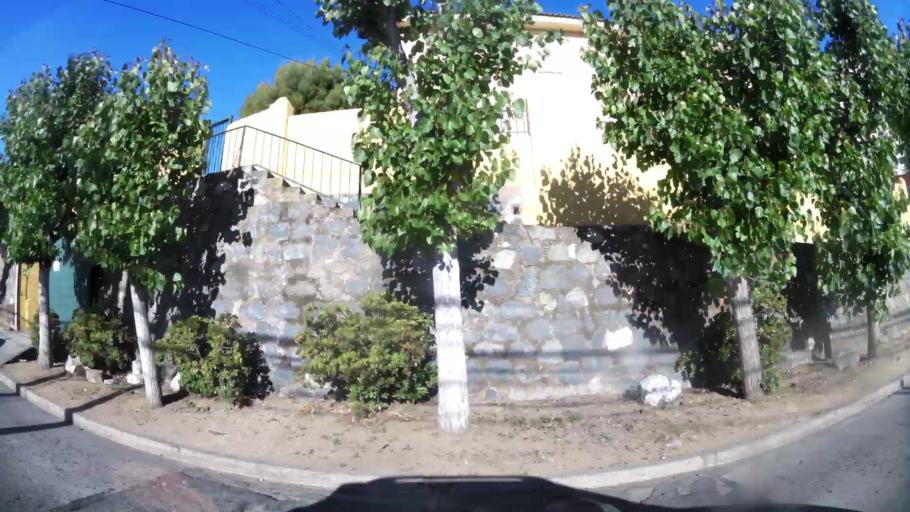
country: CL
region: Valparaiso
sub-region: Provincia de Valparaiso
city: Vina del Mar
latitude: -33.0289
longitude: -71.5843
